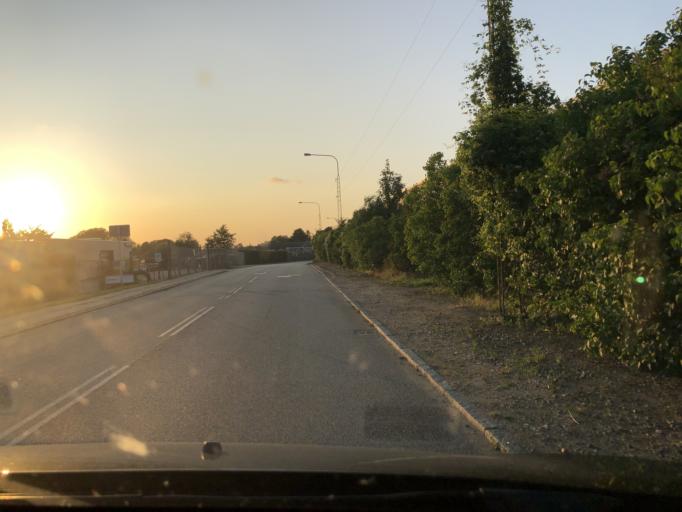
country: DK
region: South Denmark
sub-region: Middelfart Kommune
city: Middelfart
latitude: 55.5042
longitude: 9.7554
